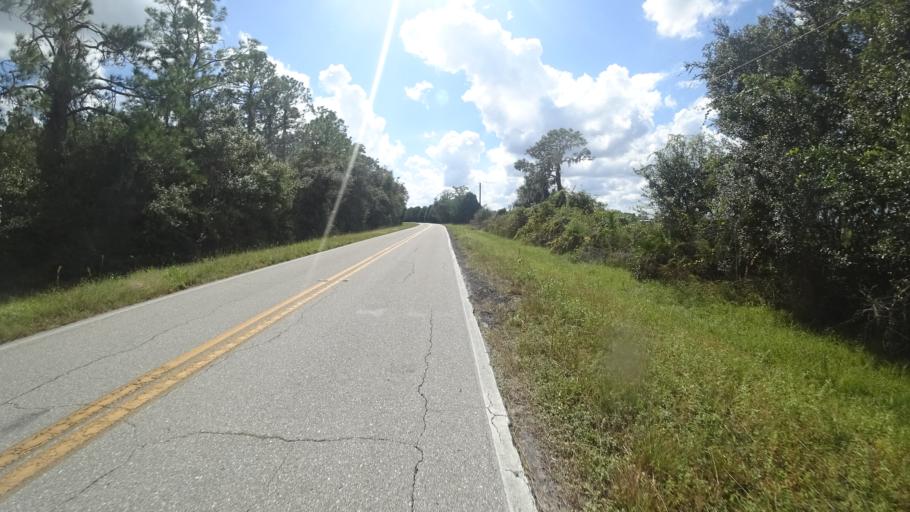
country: US
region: Florida
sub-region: Sarasota County
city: Warm Mineral Springs
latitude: 27.2601
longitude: -82.1213
